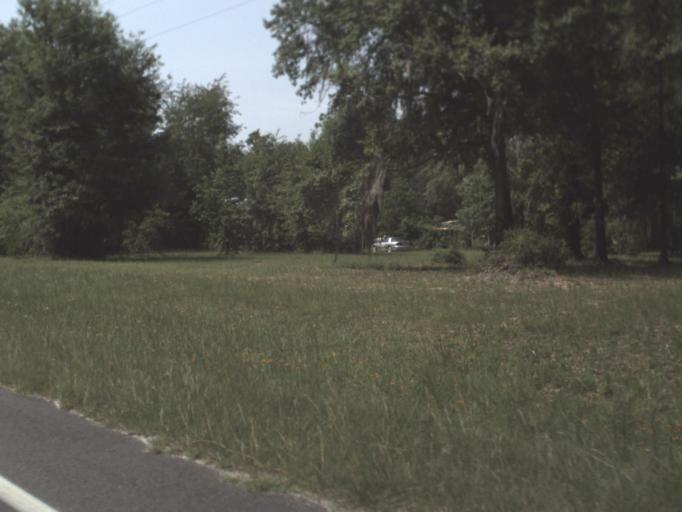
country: US
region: Georgia
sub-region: Echols County
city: Statenville
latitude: 30.6018
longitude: -83.0150
